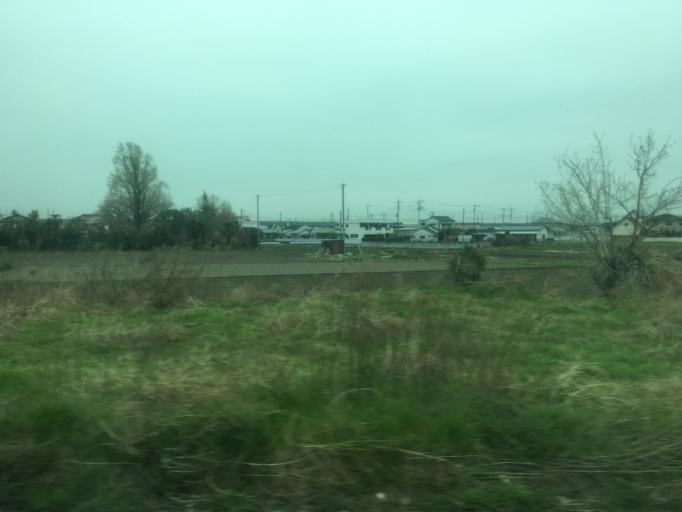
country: JP
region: Saitama
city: Kumagaya
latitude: 36.1267
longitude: 139.4118
